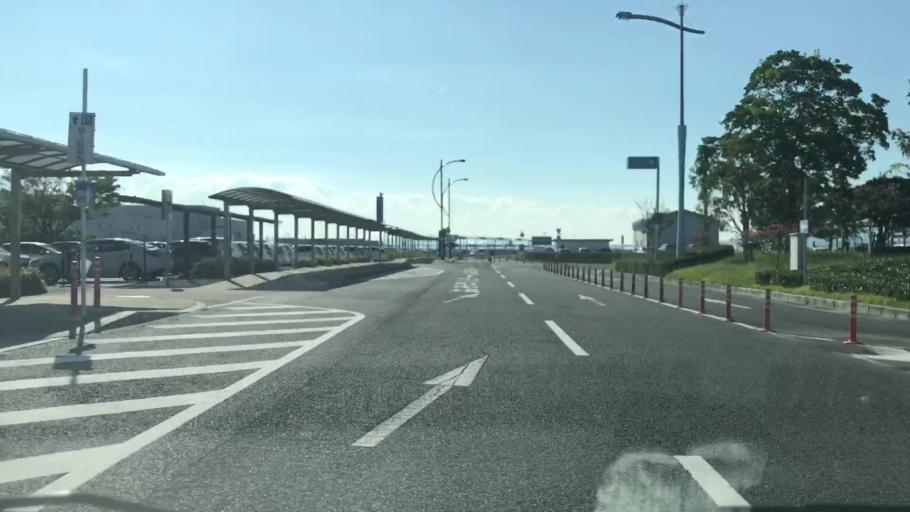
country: JP
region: Saga Prefecture
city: Okawa
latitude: 33.1538
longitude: 130.3026
